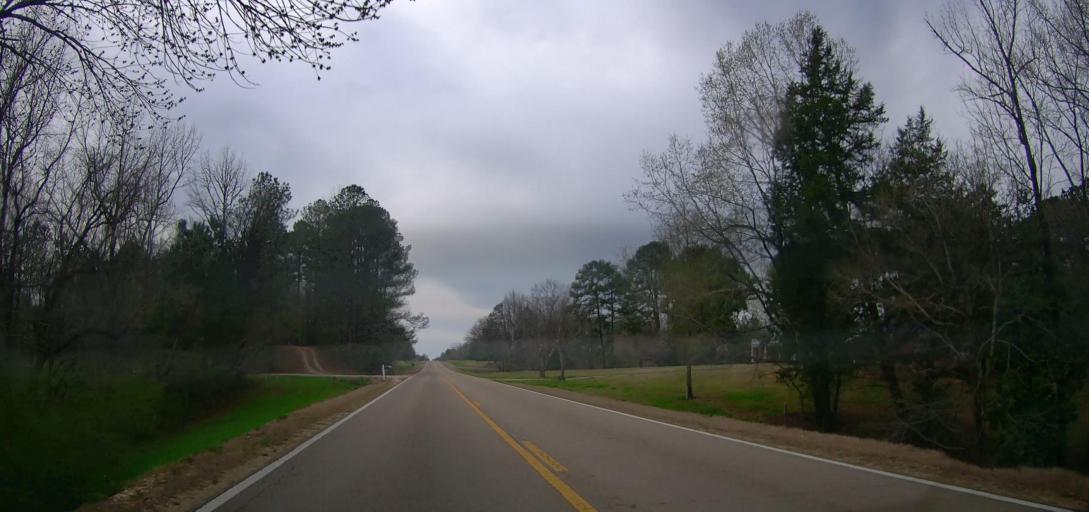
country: US
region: Mississippi
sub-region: Itawamba County
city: Mantachie
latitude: 34.2596
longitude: -88.5161
